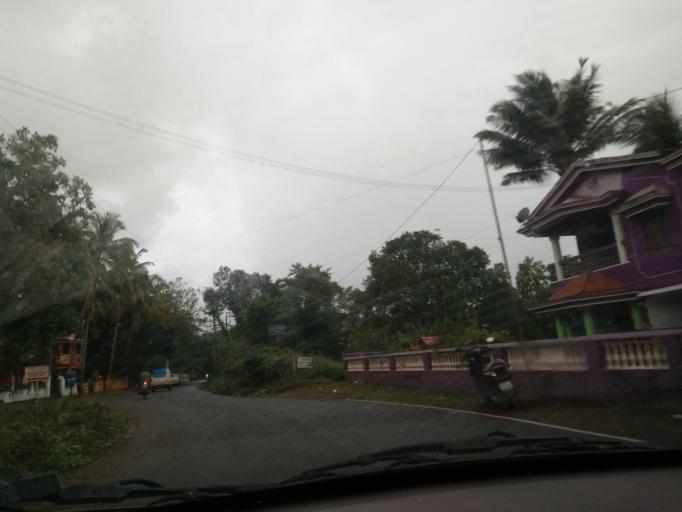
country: IN
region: Goa
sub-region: South Goa
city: Chinchinim
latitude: 15.2438
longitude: 73.9788
